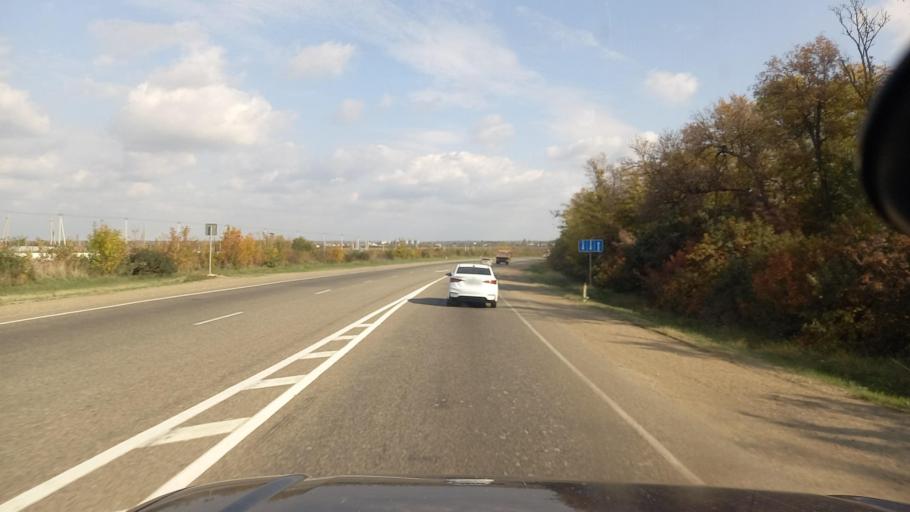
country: RU
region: Krasnodarskiy
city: Akhtyrskiy
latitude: 44.8499
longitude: 38.3163
